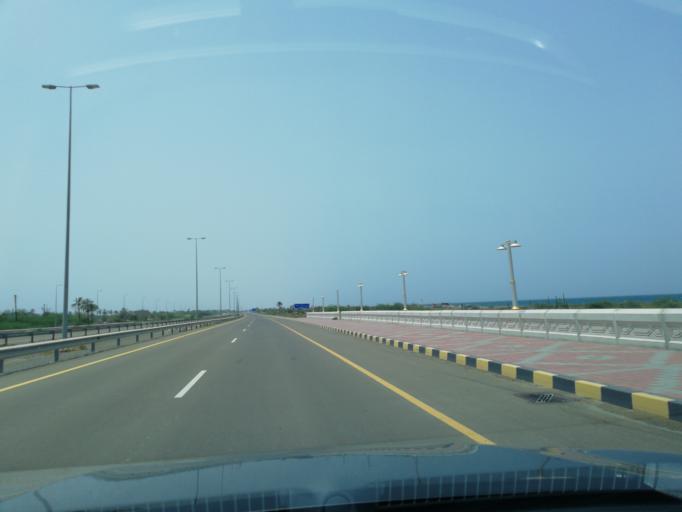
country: OM
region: Al Batinah
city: Al Liwa'
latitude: 24.6298
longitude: 56.5283
